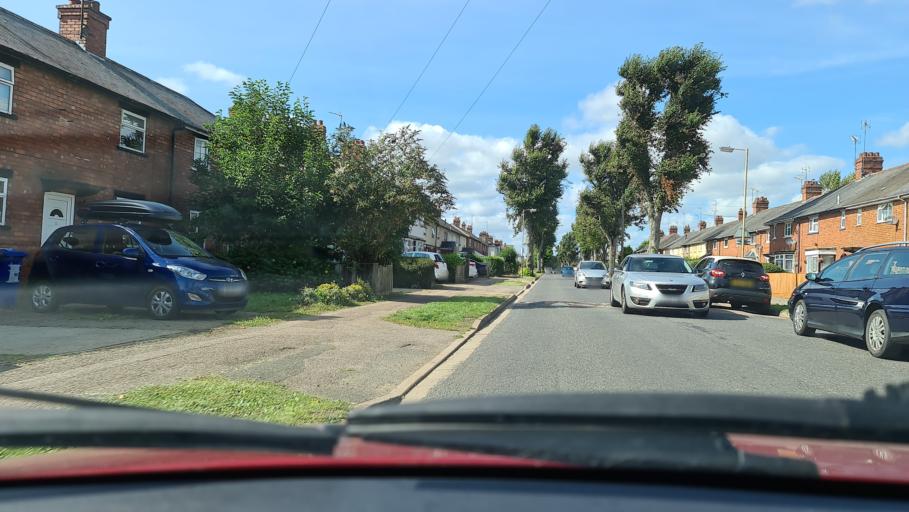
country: GB
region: England
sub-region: Oxfordshire
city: Banbury
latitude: 52.0499
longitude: -1.3408
